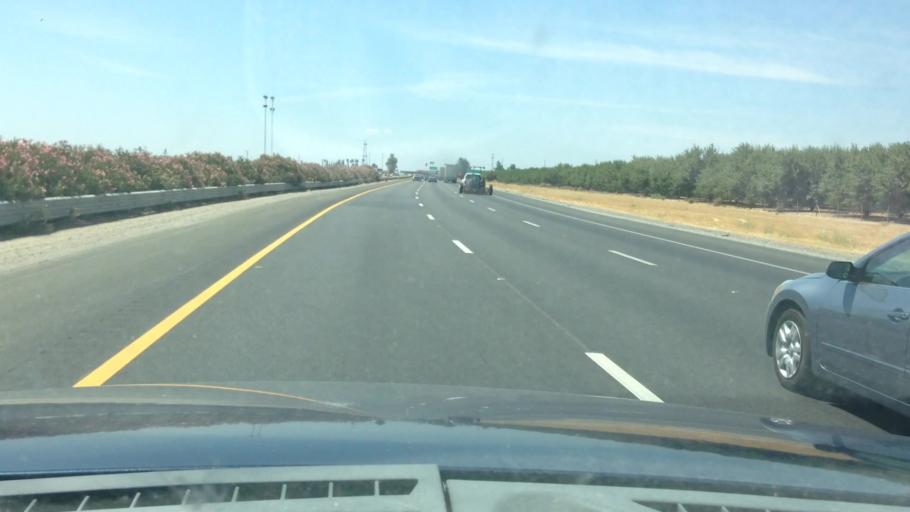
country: US
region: California
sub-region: Kern County
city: McFarland
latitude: 35.6138
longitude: -119.2126
